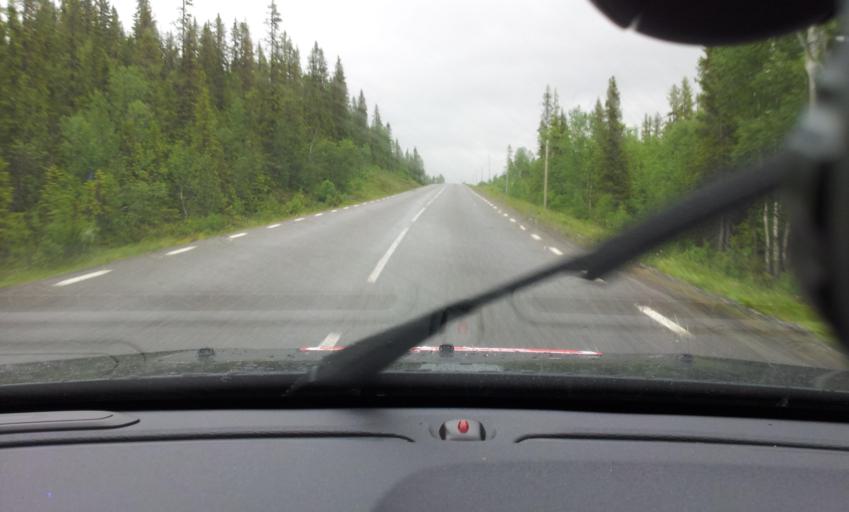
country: SE
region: Jaemtland
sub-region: Are Kommun
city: Are
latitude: 63.2260
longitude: 13.1435
